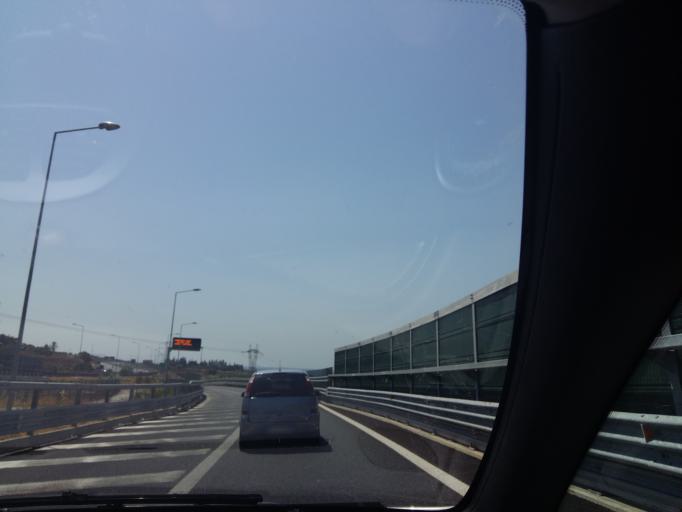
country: IT
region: Calabria
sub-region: Provincia di Reggio Calabria
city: Campo Calabro
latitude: 38.2078
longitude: 15.6410
